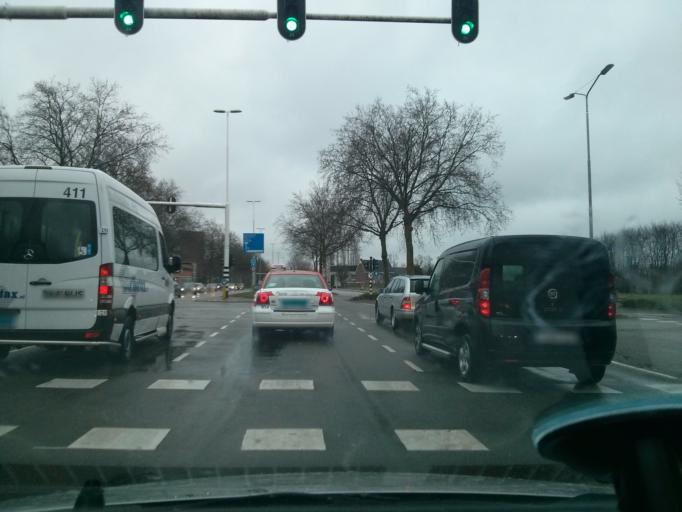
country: NL
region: North Brabant
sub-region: Gemeente Eindhoven
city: Eindhoven
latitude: 51.4276
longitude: 5.4637
